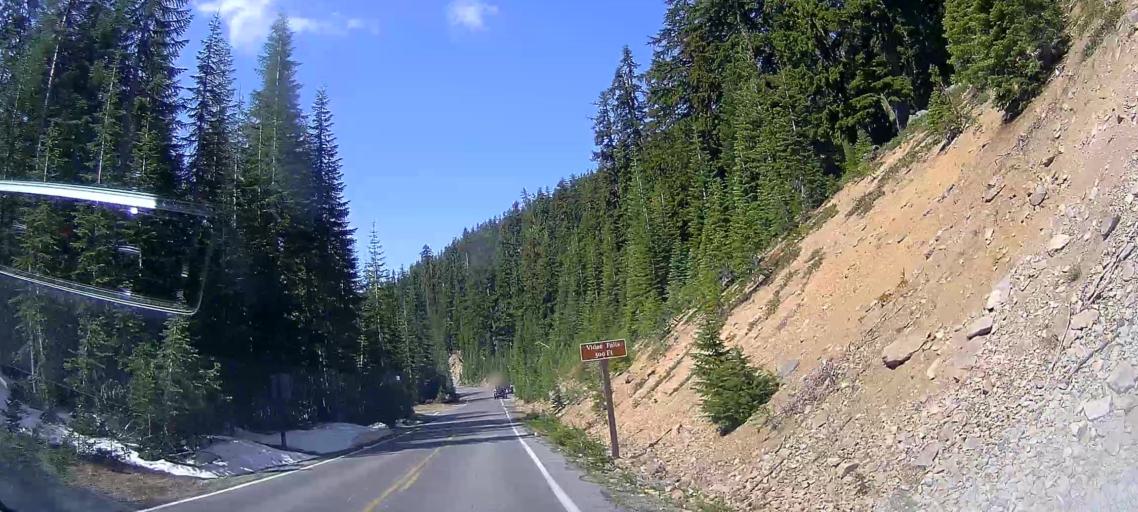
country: US
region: Oregon
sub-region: Klamath County
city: Klamath Falls
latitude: 42.8848
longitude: -122.0981
